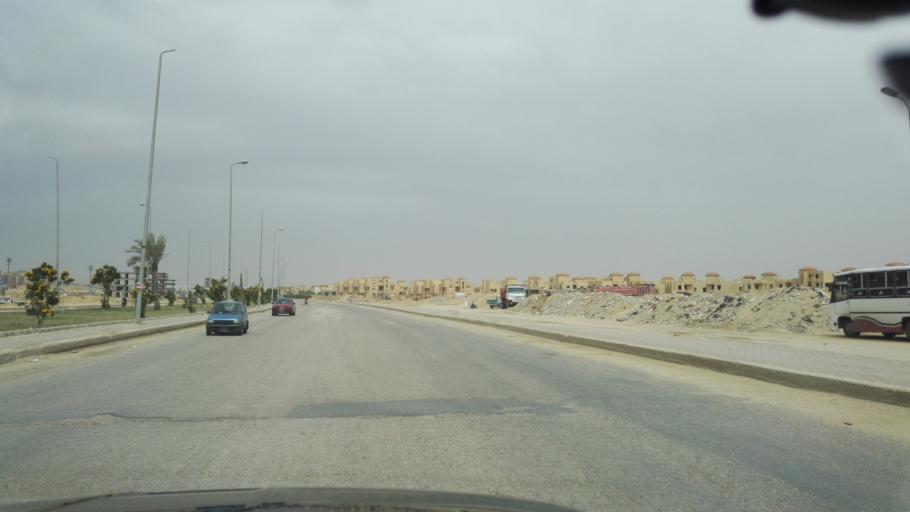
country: EG
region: Muhafazat al Qalyubiyah
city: Al Khankah
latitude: 30.0183
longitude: 31.5274
